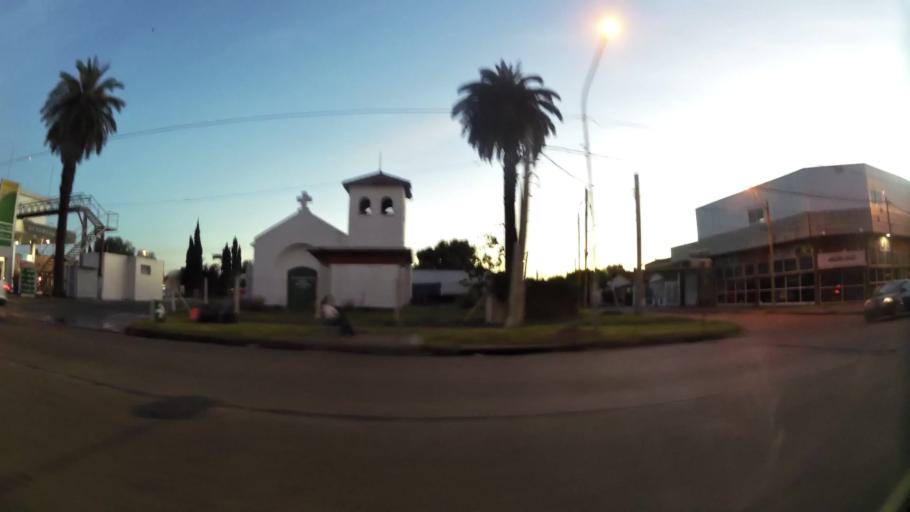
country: AR
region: Buenos Aires
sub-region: Partido de Moron
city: Moron
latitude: -34.6590
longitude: -58.6364
